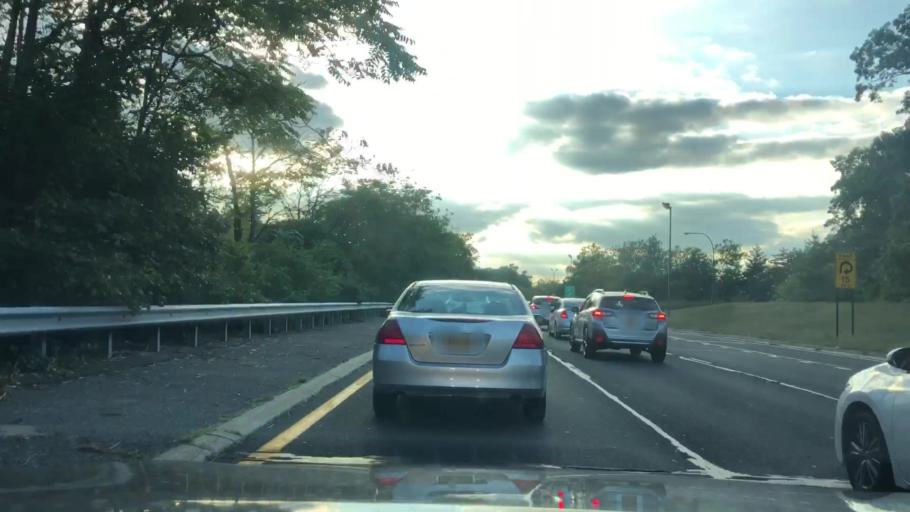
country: US
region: New York
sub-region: Nassau County
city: North Merrick
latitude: 40.6908
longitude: -73.5780
